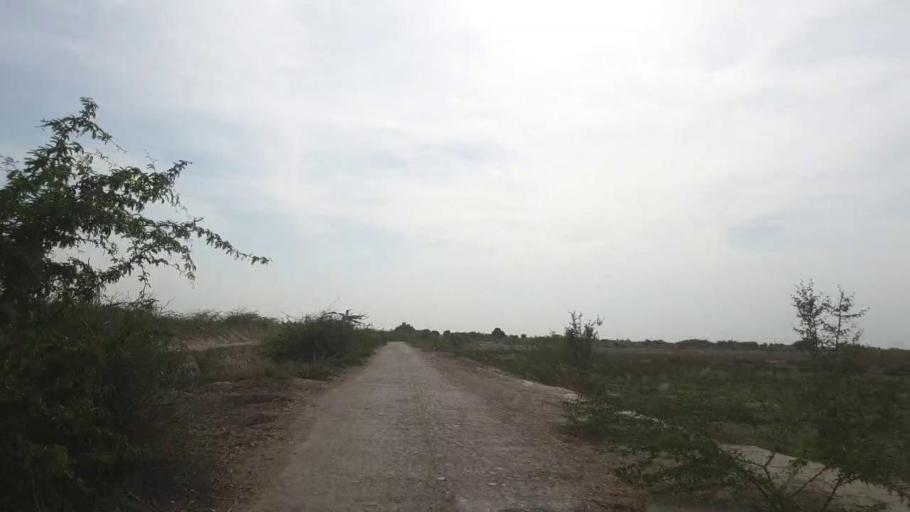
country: PK
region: Sindh
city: Nabisar
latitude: 24.9956
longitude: 69.5579
